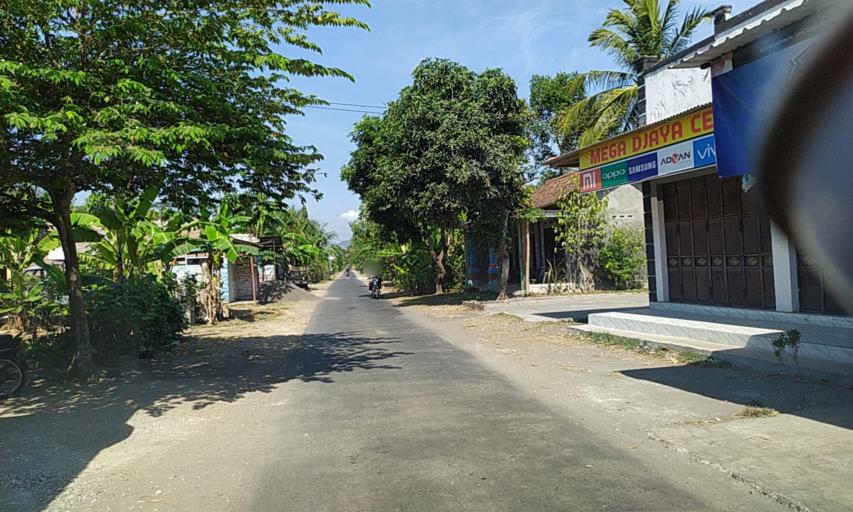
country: ID
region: Central Java
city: Kroya
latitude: -7.6793
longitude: 109.3424
